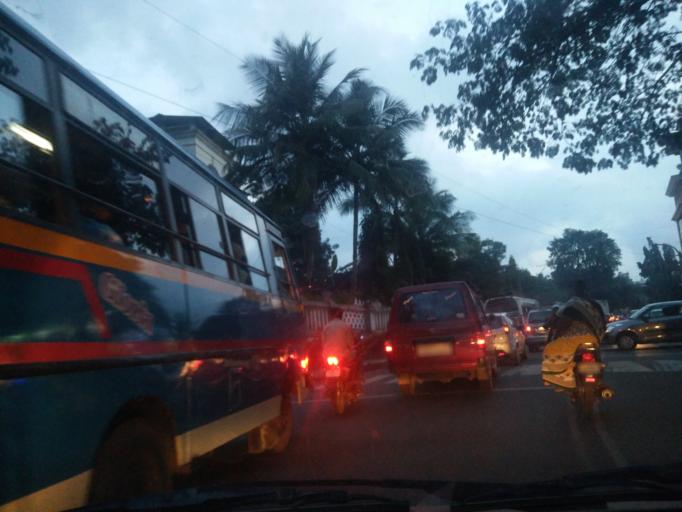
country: IN
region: Goa
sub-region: South Goa
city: Madgaon
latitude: 15.2803
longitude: 73.9605
